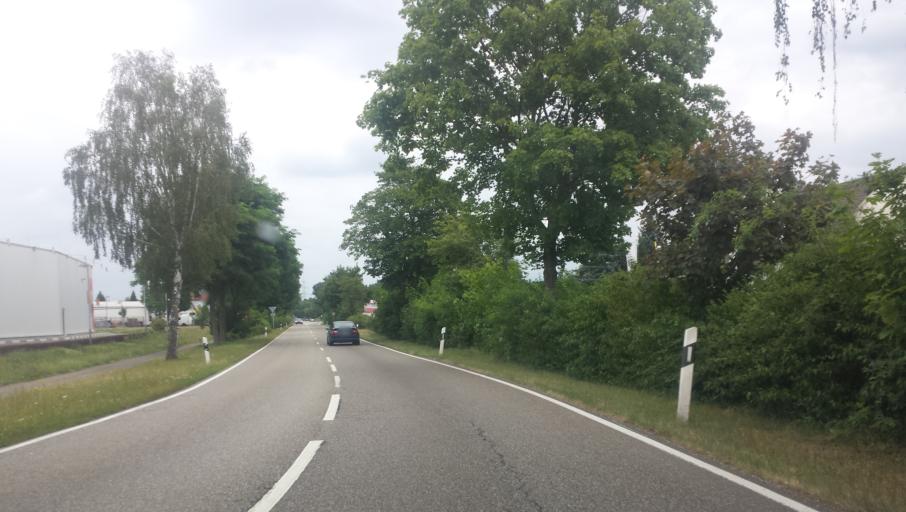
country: DE
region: Rheinland-Pfalz
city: Bellheim
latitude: 49.1947
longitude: 8.2995
